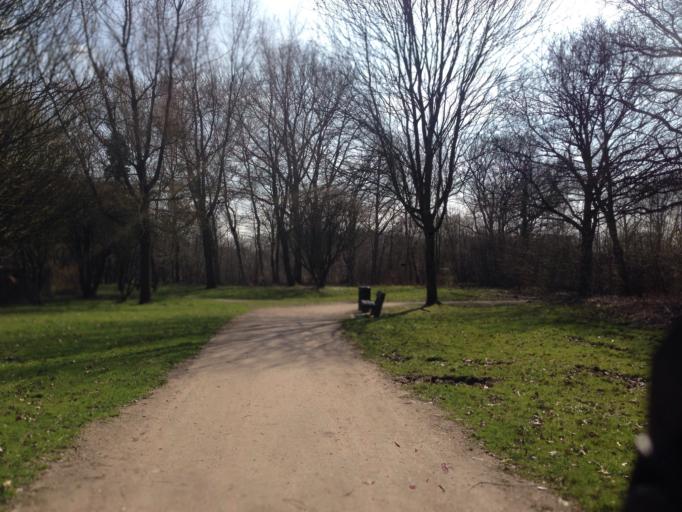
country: DE
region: Schleswig-Holstein
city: Barsbuettel
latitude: 53.5800
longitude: 10.1522
